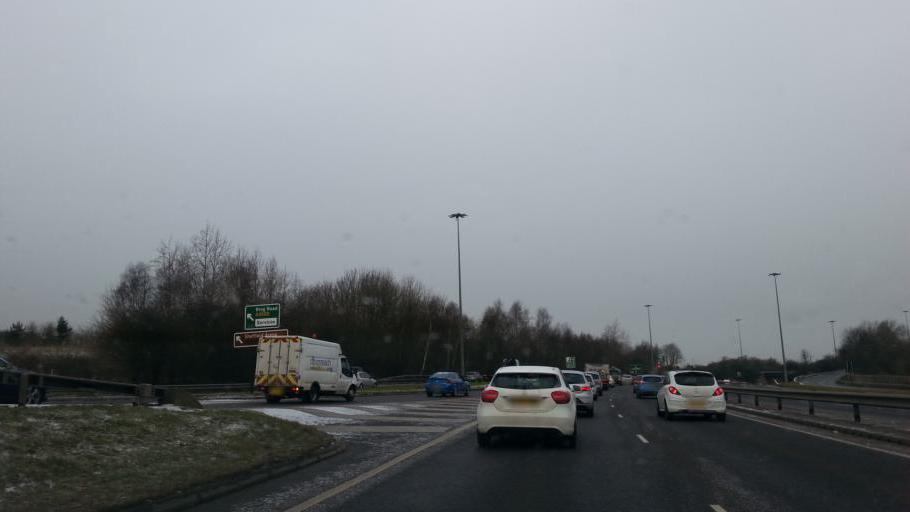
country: GB
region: England
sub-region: Rotherham
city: Orgreave
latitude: 53.3744
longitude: -1.4092
